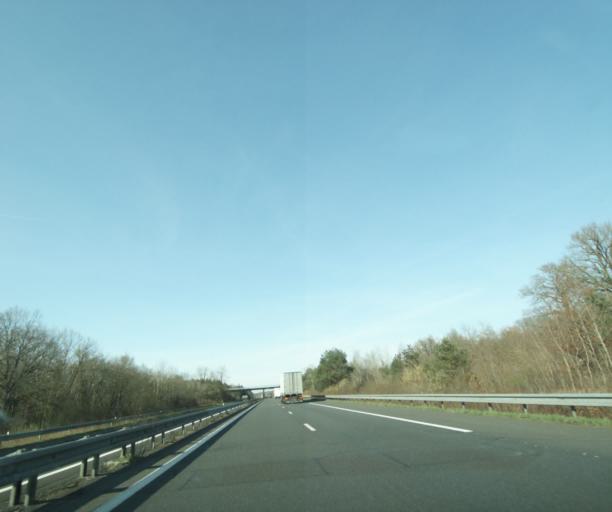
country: FR
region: Centre
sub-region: Departement du Loiret
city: Jouy-le-Potier
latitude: 47.7656
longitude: 1.8525
